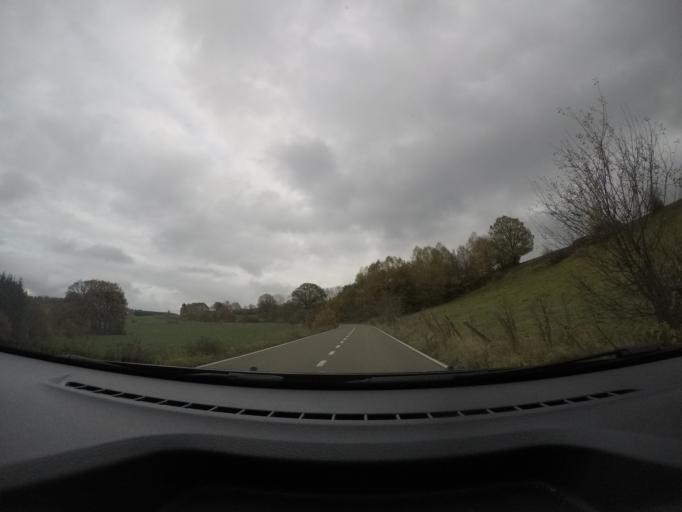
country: BE
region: Wallonia
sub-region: Province du Luxembourg
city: Bertogne
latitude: 50.1413
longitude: 5.6947
